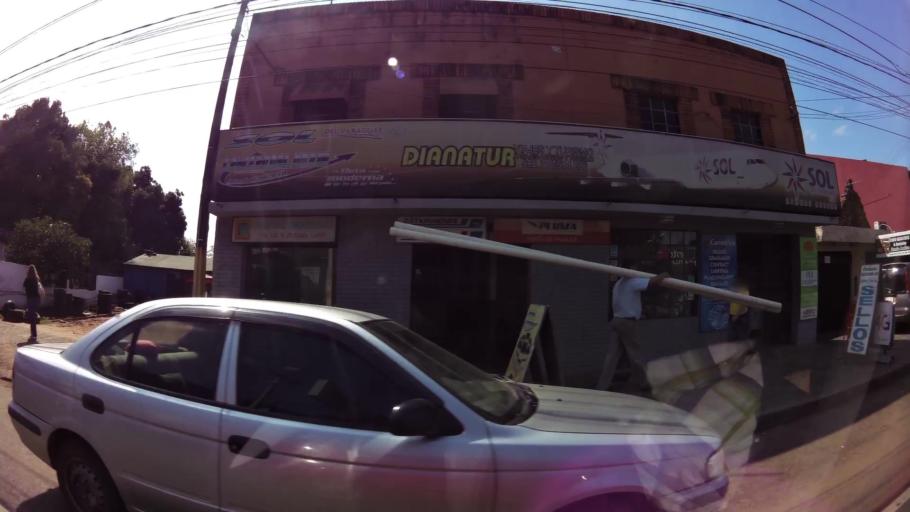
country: PY
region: Central
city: San Lorenzo
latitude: -25.3433
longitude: -57.5038
